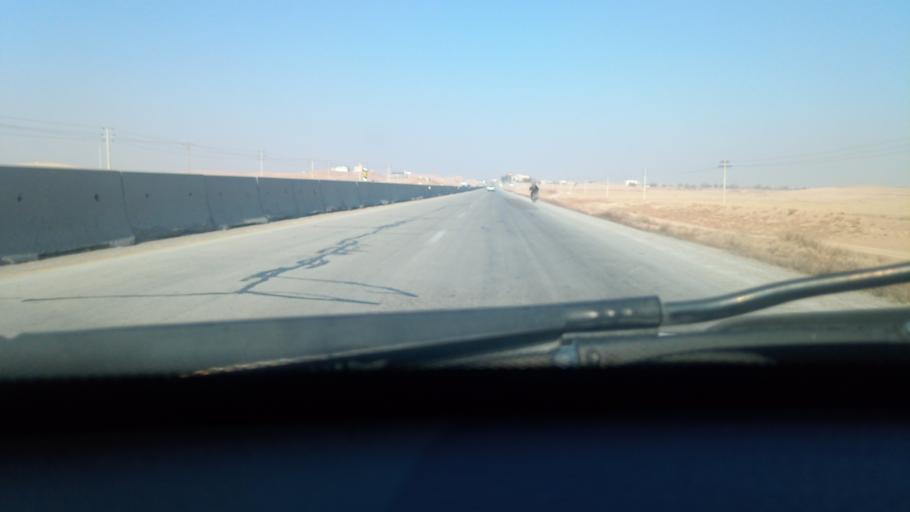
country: IR
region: Razavi Khorasan
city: Quchan
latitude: 36.9297
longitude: 58.6922
